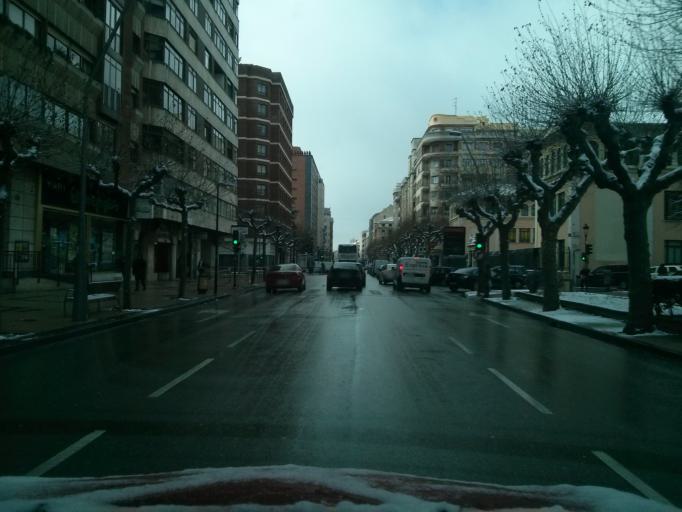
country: ES
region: Castille and Leon
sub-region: Provincia de Burgos
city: Burgos
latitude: 42.3424
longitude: -3.6940
